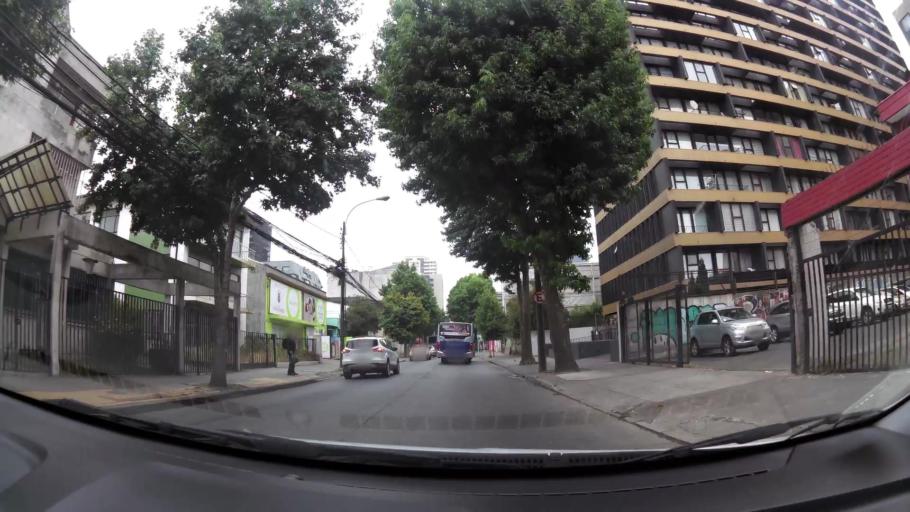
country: CL
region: Biobio
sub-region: Provincia de Concepcion
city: Concepcion
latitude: -36.8237
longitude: -73.0407
